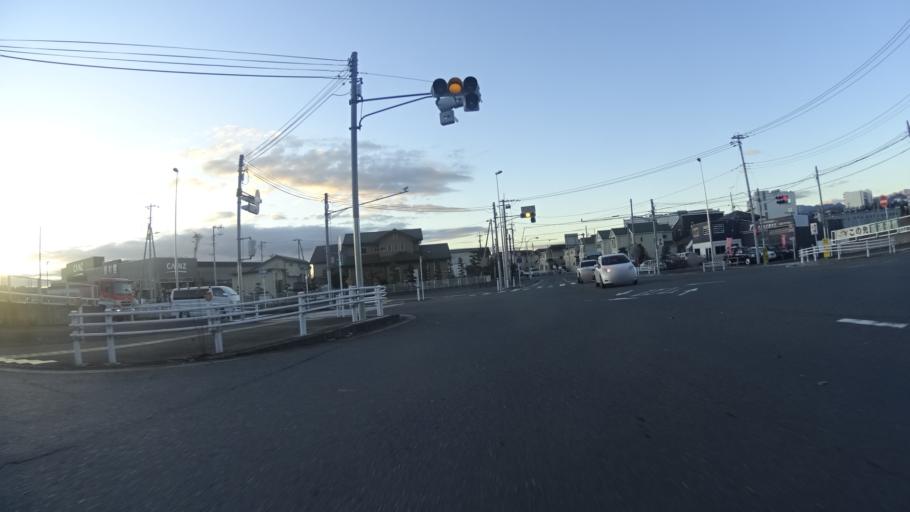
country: JP
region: Kanagawa
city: Zama
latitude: 35.5270
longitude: 139.3651
